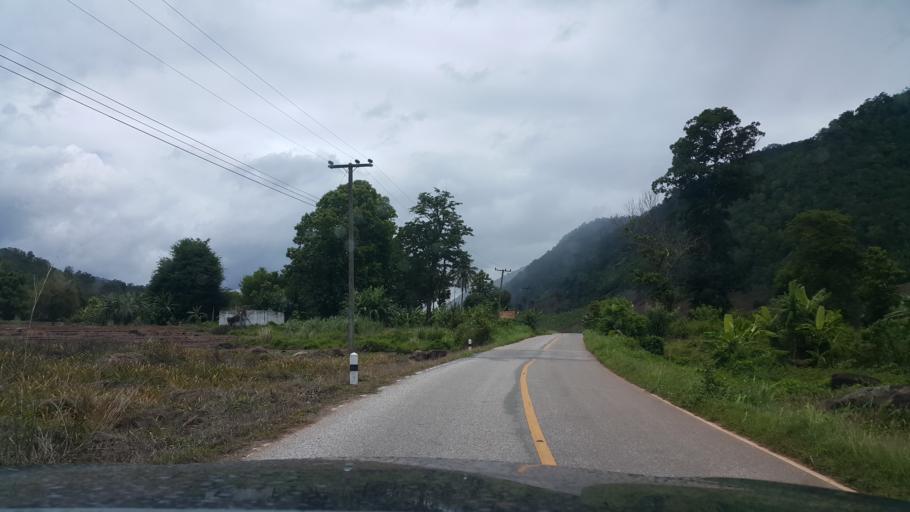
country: TH
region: Loei
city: Na Haeo
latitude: 17.5474
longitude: 100.8402
